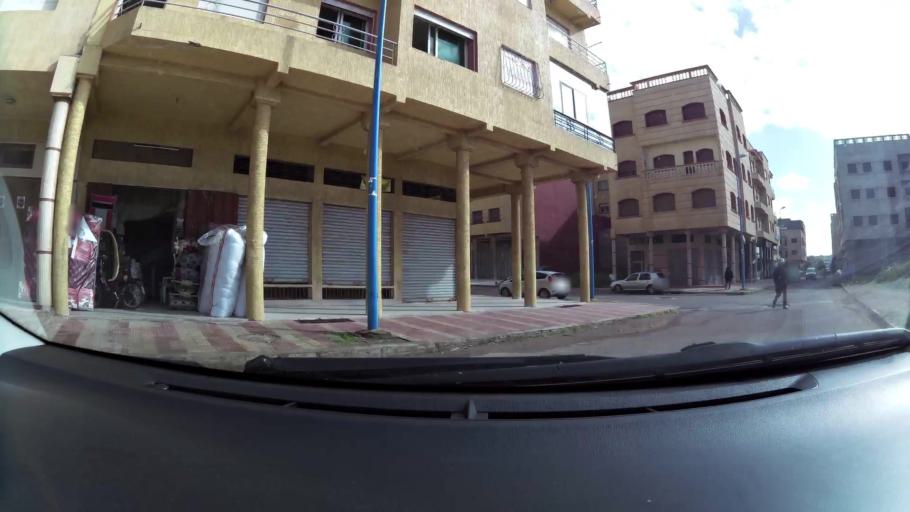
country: MA
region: Grand Casablanca
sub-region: Mohammedia
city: Mohammedia
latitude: 33.7003
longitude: -7.3617
